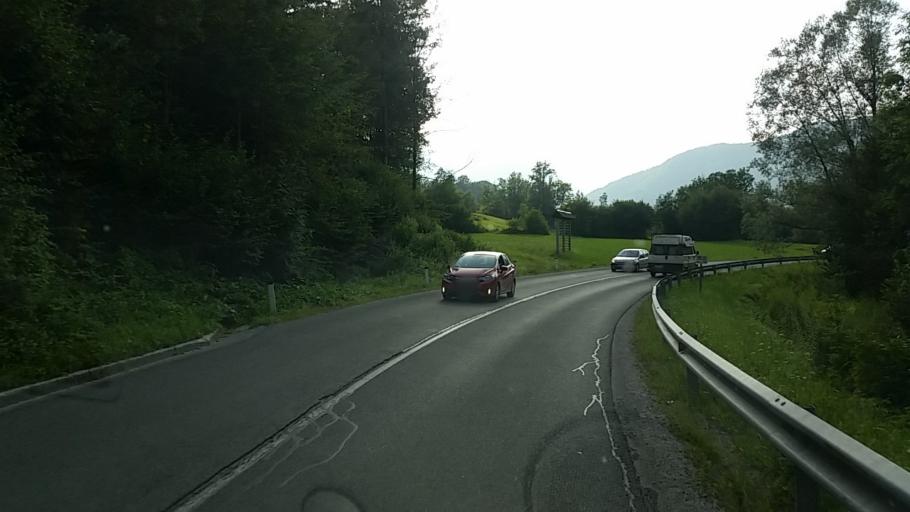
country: SI
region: Bohinj
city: Bohinjska Bistrica
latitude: 46.2728
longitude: 13.9414
